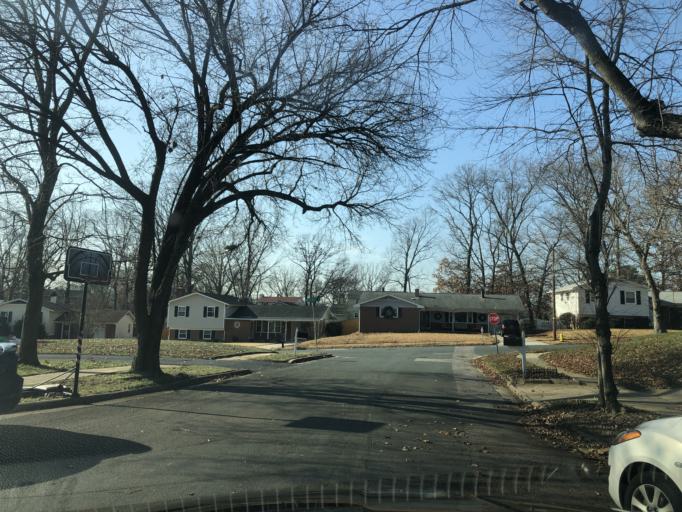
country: US
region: Maryland
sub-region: Anne Arundel County
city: Odenton
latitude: 39.0730
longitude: -76.6928
